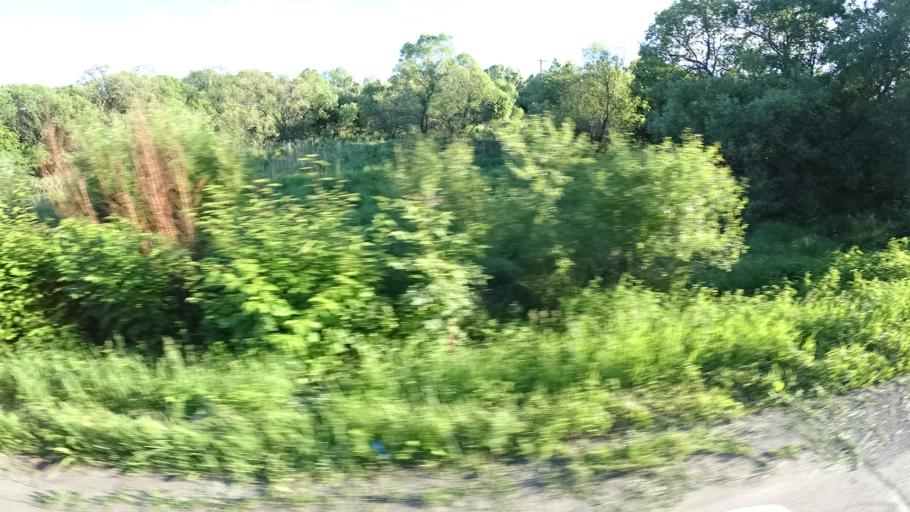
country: RU
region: Khabarovsk Krai
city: Khor
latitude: 47.8537
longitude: 134.9741
